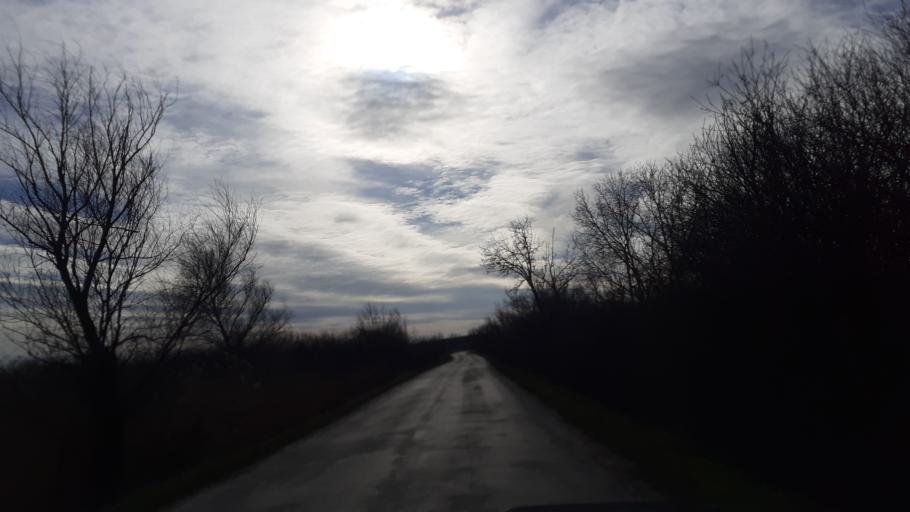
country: HU
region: Fejer
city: Kaloz
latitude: 46.9127
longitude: 18.5372
